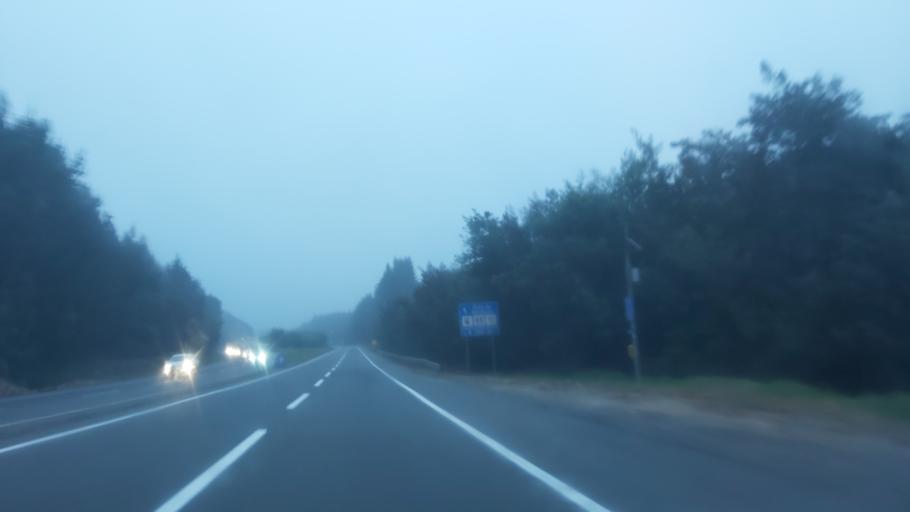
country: CL
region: Biobio
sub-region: Provincia de Concepcion
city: Penco
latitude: -36.7439
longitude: -72.9138
